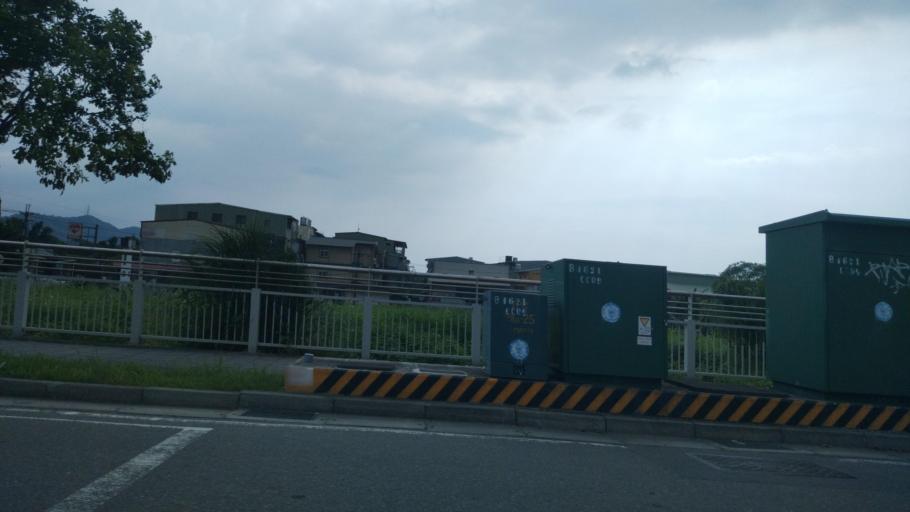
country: TW
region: Taiwan
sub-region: Taoyuan
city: Taoyuan
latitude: 24.9528
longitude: 121.3747
